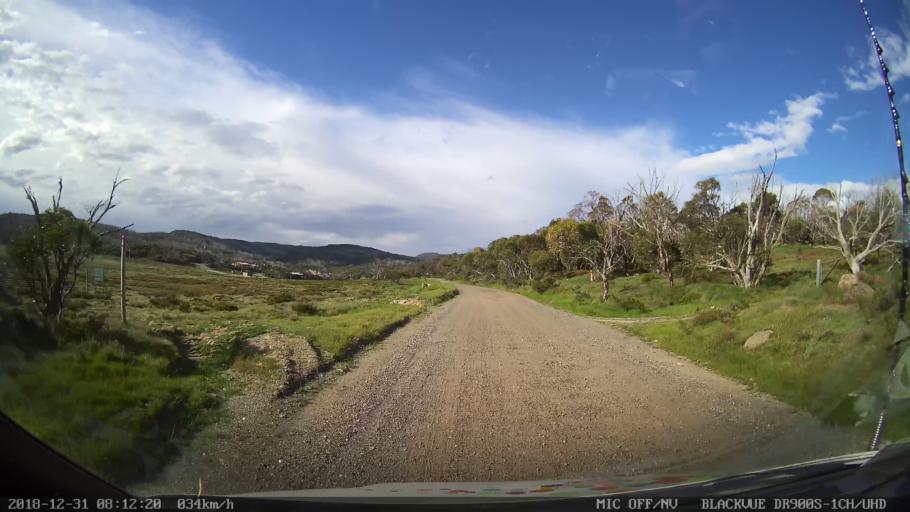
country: AU
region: New South Wales
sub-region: Snowy River
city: Jindabyne
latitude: -36.3869
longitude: 148.4301
